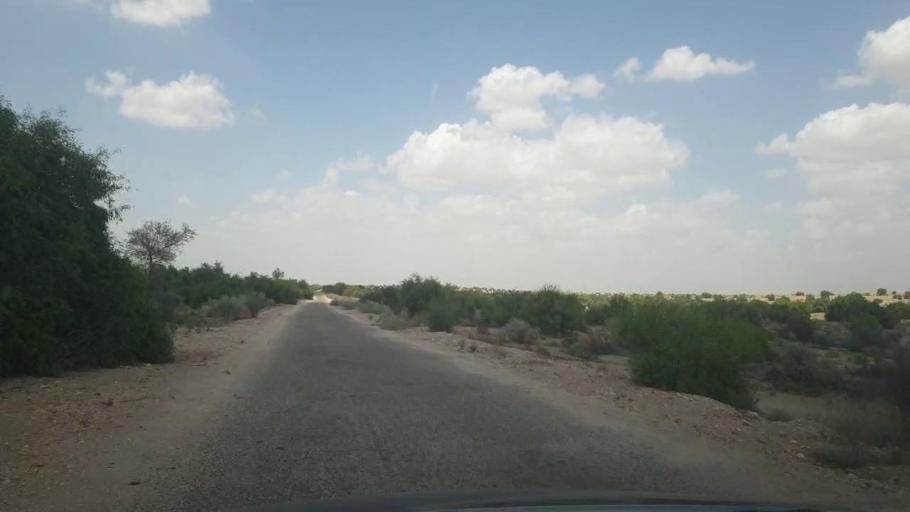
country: PK
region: Sindh
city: Kot Diji
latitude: 27.2245
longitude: 69.1105
